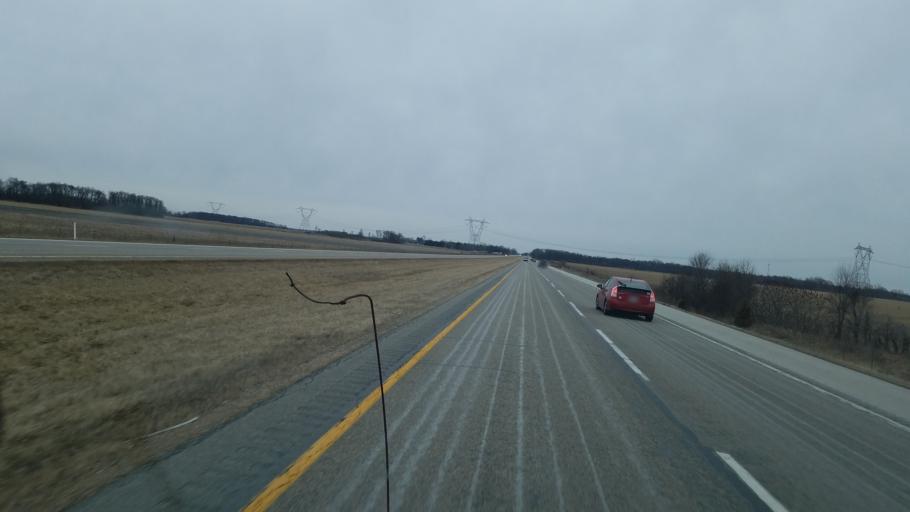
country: US
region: Indiana
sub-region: LaPorte County
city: Wanatah
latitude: 41.4287
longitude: -86.8038
